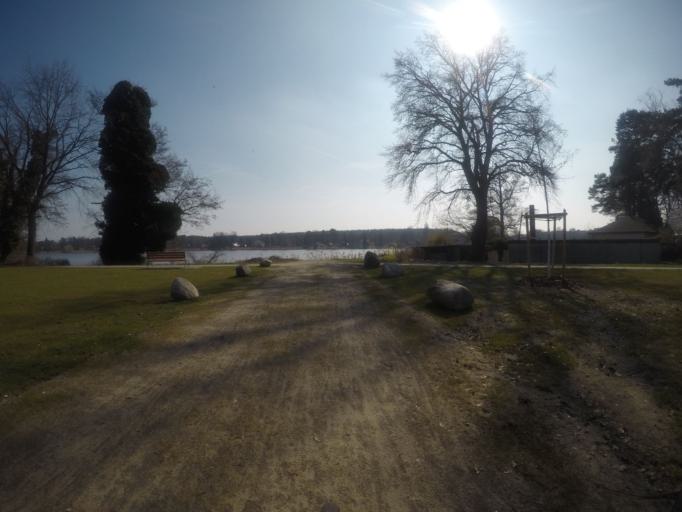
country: DE
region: Brandenburg
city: Konigs Wusterhausen
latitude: 52.2924
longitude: 13.6843
